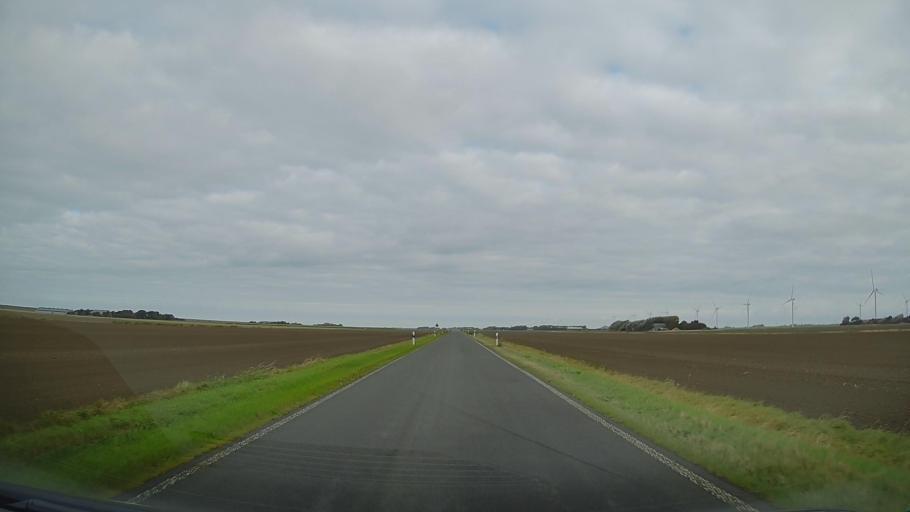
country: DE
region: Schleswig-Holstein
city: Friedrich-Wilhelm-Lubke-Koog
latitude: 54.8438
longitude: 8.6220
